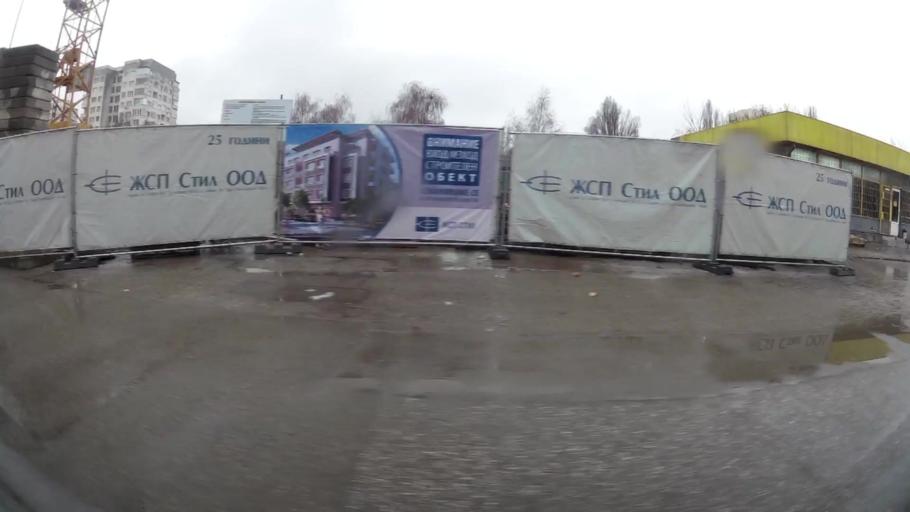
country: BG
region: Sofia-Capital
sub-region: Stolichna Obshtina
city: Sofia
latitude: 42.6698
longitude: 23.3898
